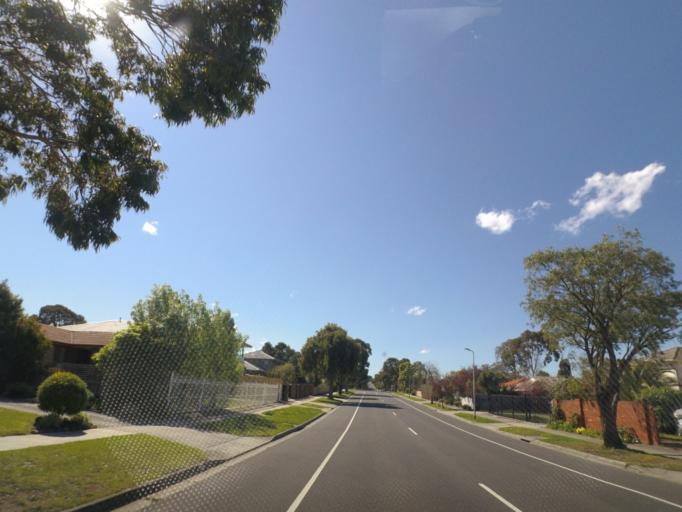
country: AU
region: Victoria
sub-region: Knox
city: Wantirna
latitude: -37.8634
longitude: 145.2255
